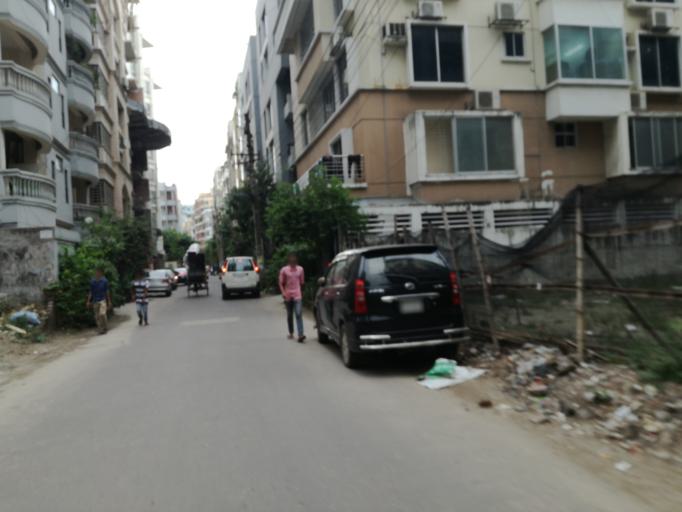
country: BD
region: Dhaka
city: Paltan
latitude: 23.7731
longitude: 90.4130
